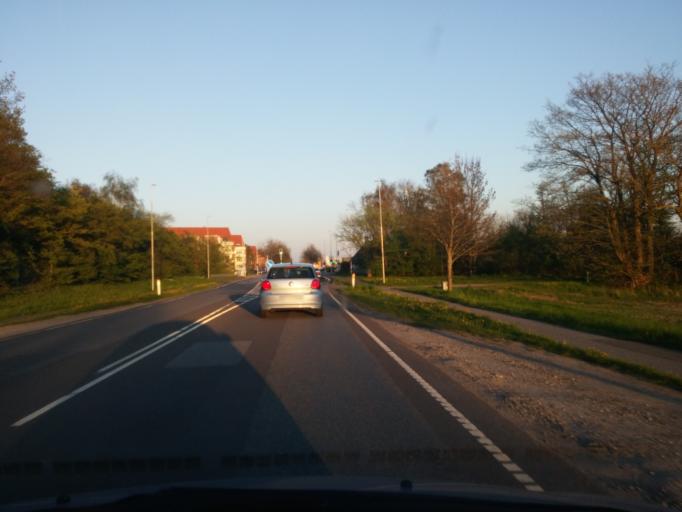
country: DK
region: South Denmark
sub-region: Nyborg Kommune
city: Nyborg
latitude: 55.3207
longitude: 10.7762
